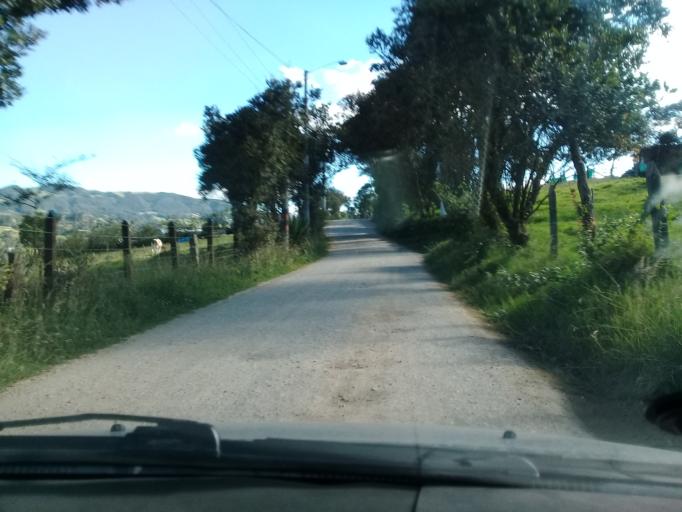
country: CO
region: Cundinamarca
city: Zipaquira
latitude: 4.9933
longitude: -74.0683
